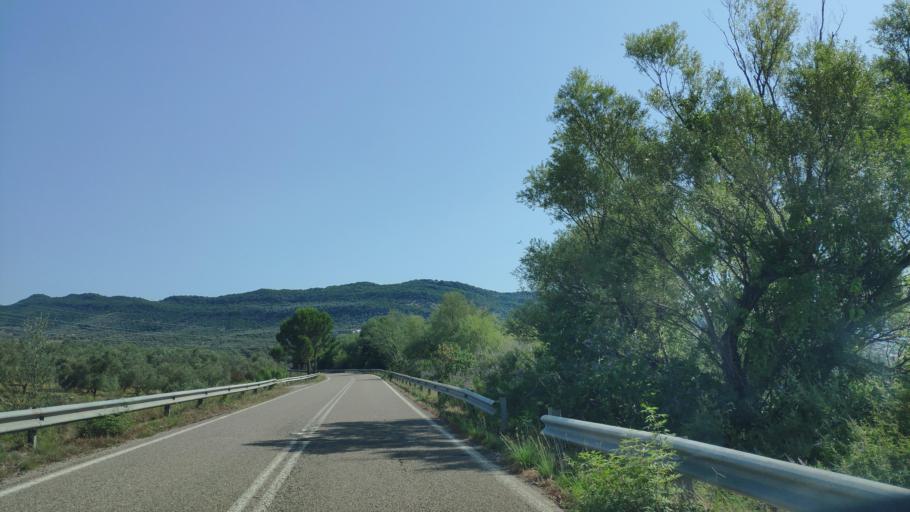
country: GR
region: West Greece
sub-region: Nomos Aitolias kai Akarnanias
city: Lepenou
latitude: 38.7037
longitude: 21.3221
